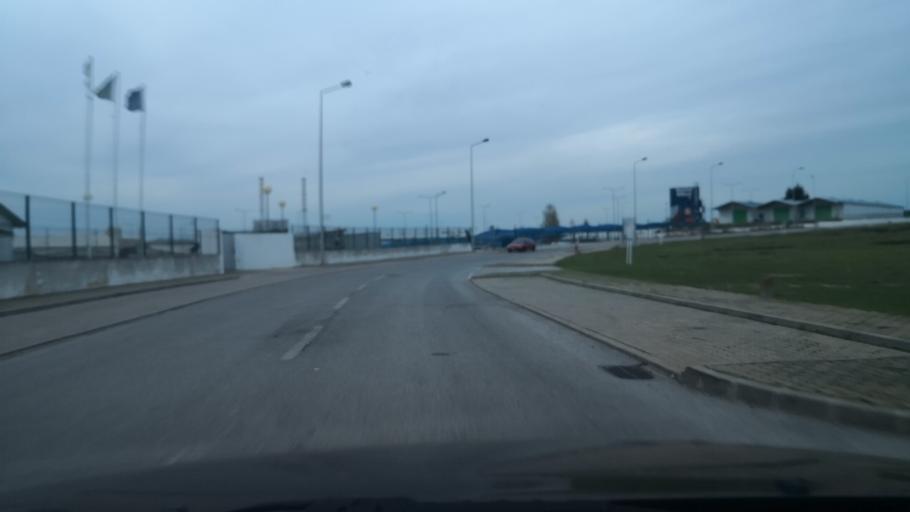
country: PT
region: Setubal
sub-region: Setubal
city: Setubal
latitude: 38.4971
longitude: -8.8290
